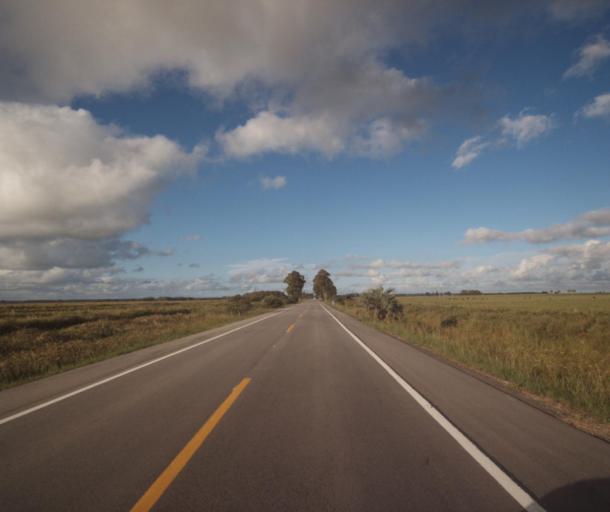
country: BR
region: Rio Grande do Sul
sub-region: Rio Grande
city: Rio Grande
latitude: -32.1390
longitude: -52.3789
